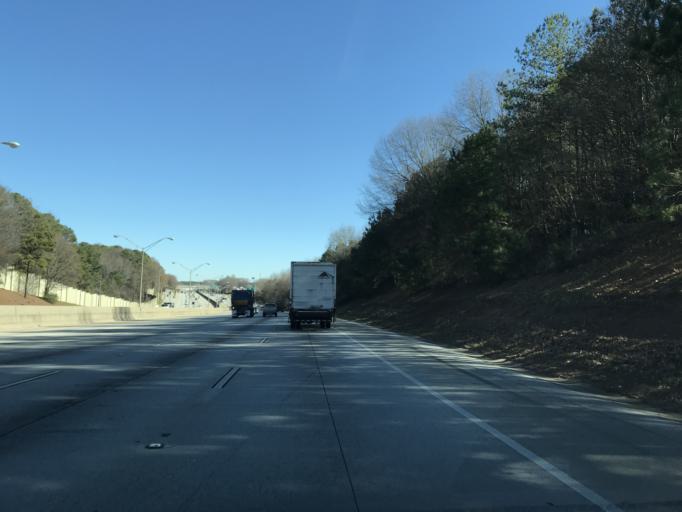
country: US
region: Georgia
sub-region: DeKalb County
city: Panthersville
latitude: 33.7122
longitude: -84.2803
